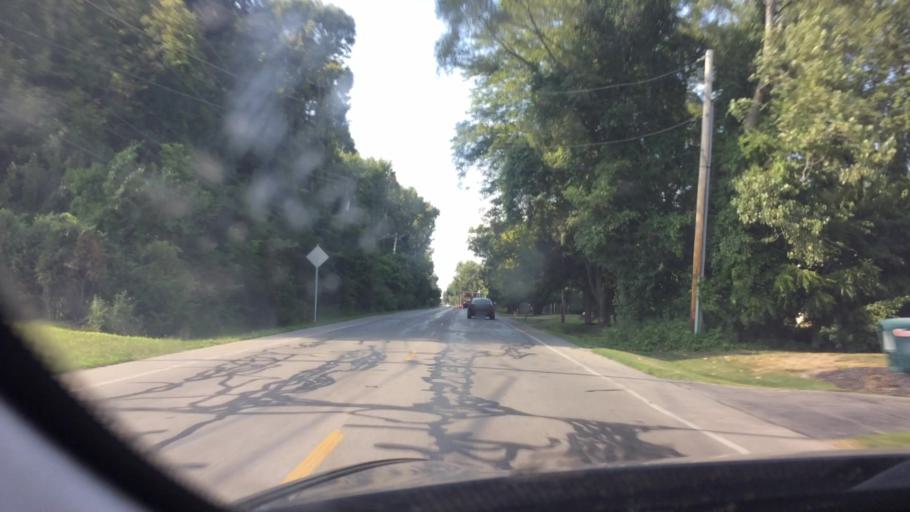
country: US
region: Ohio
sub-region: Lucas County
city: Holland
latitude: 41.6563
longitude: -83.7222
